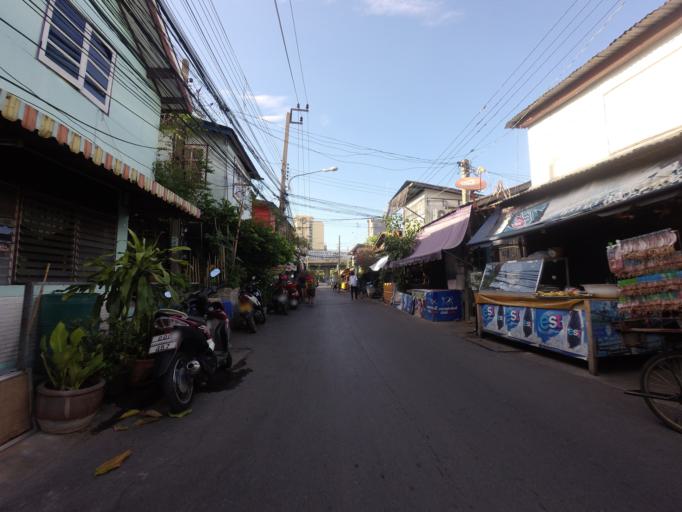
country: TH
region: Bangkok
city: Khlong Toei
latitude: 13.7113
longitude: 100.5765
